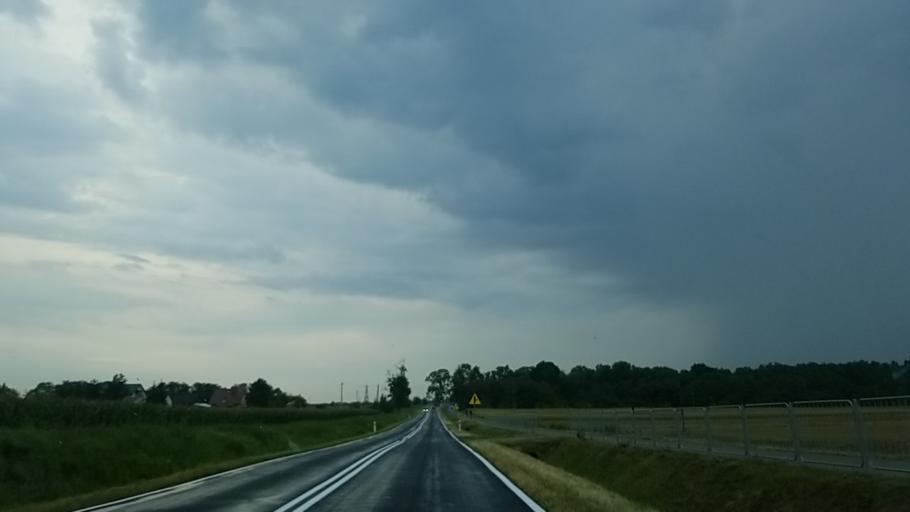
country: PL
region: Lublin Voivodeship
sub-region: Powiat wlodawski
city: Wlodawa
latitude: 51.6040
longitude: 23.5320
